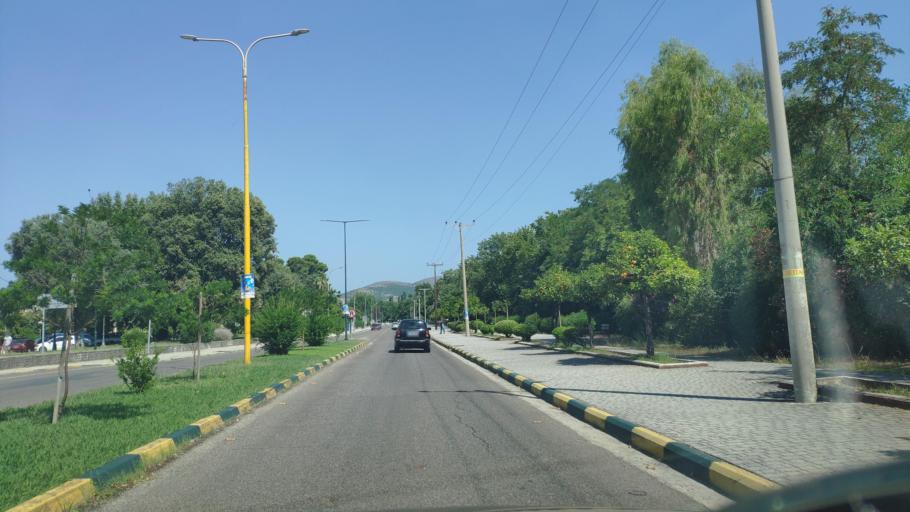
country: GR
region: Epirus
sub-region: Nomos Artas
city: Arta
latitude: 39.1637
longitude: 20.9916
